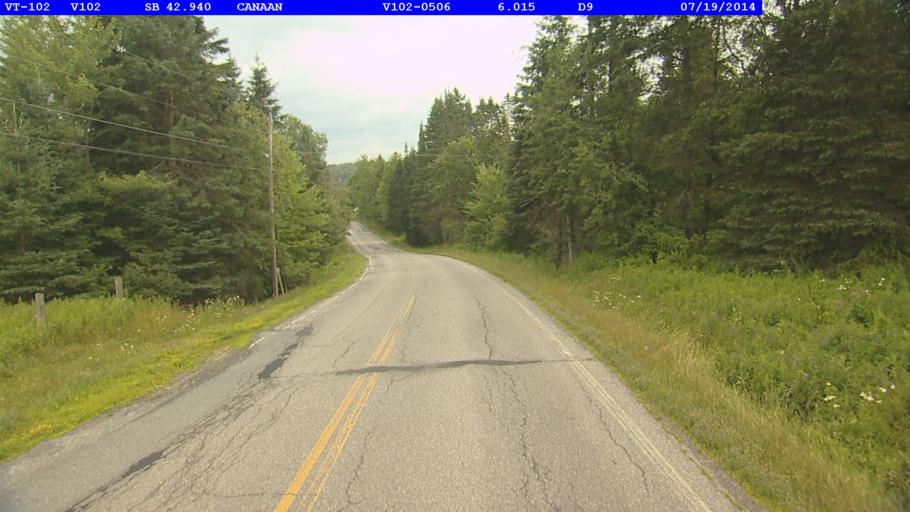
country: US
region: New Hampshire
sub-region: Coos County
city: Colebrook
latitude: 44.9853
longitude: -71.5428
